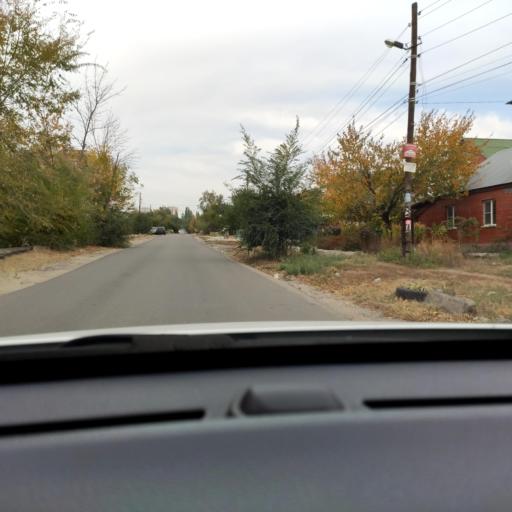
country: RU
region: Voronezj
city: Voronezh
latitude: 51.6978
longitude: 39.1689
